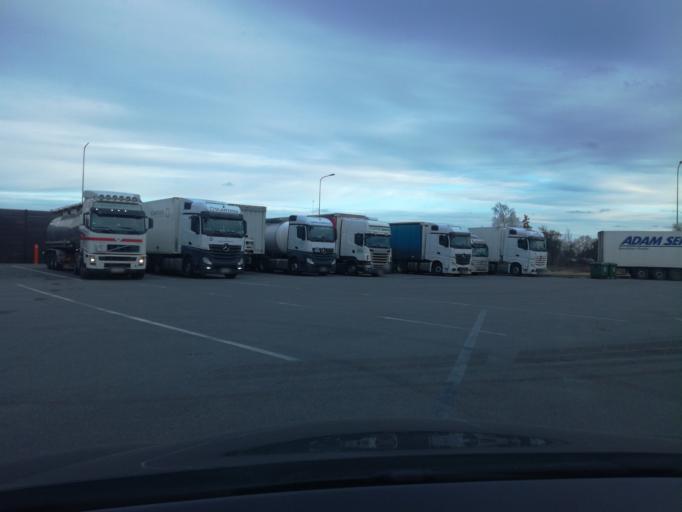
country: LT
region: Kauno apskritis
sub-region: Kauno rajonas
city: Garliava
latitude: 54.8190
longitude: 23.8584
